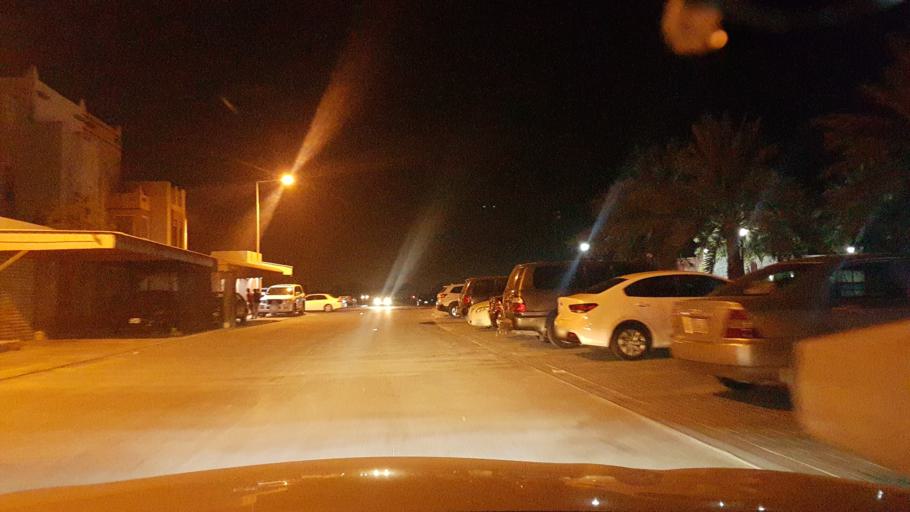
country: BH
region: Central Governorate
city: Madinat Hamad
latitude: 26.0948
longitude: 50.4795
